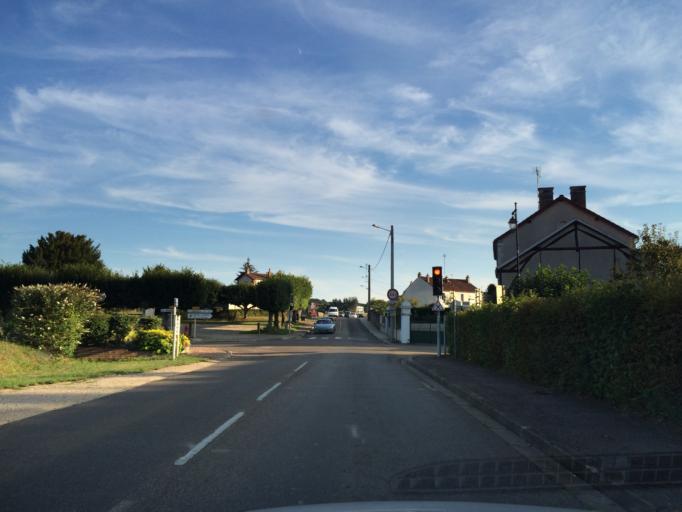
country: FR
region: Bourgogne
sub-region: Departement de l'Yonne
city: Saint-Georges-sur-Baulche
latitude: 47.8190
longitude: 3.5393
